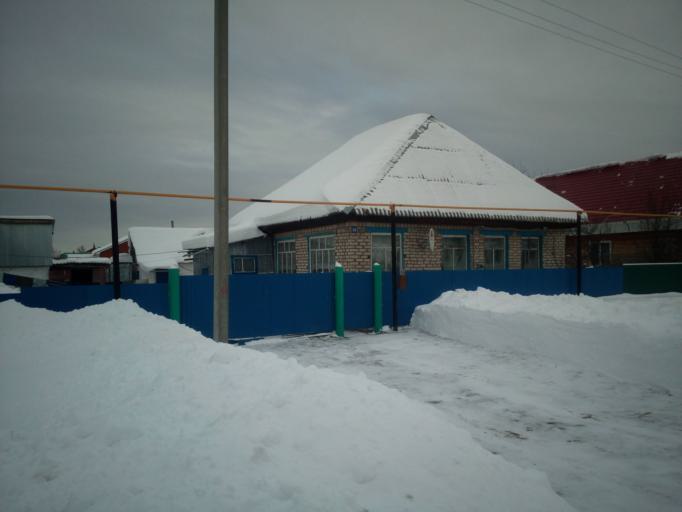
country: RU
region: Bashkortostan
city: Kaltasy
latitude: 55.8060
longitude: 54.5329
